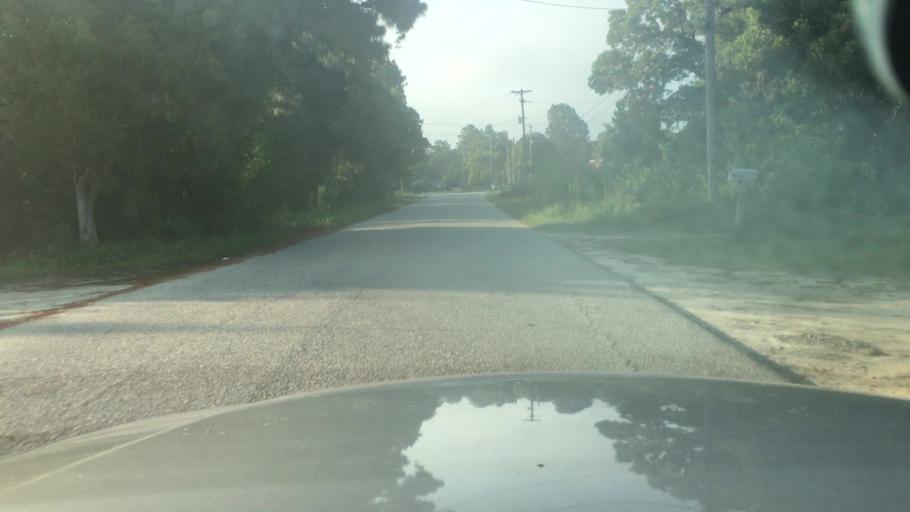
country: US
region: North Carolina
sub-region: Cumberland County
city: Spring Lake
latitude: 35.1116
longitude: -78.9359
